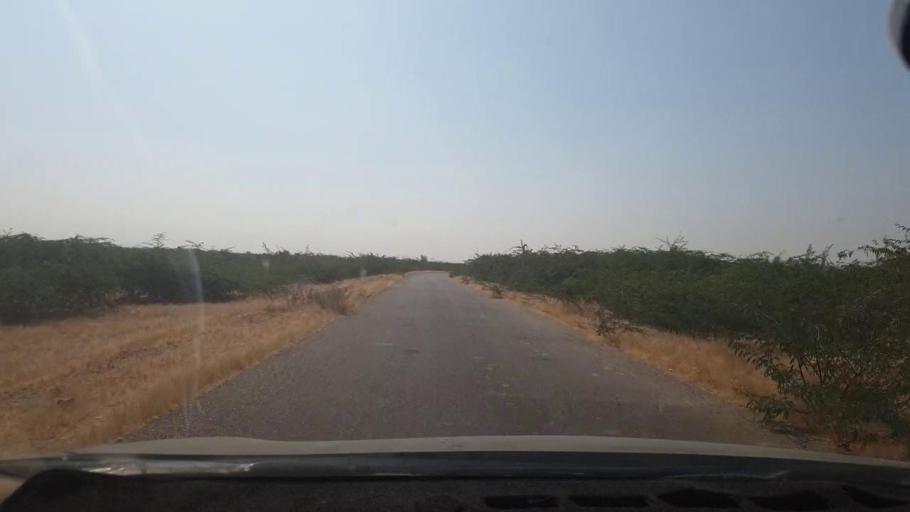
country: PK
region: Sindh
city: Malir Cantonment
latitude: 25.1593
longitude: 67.1504
